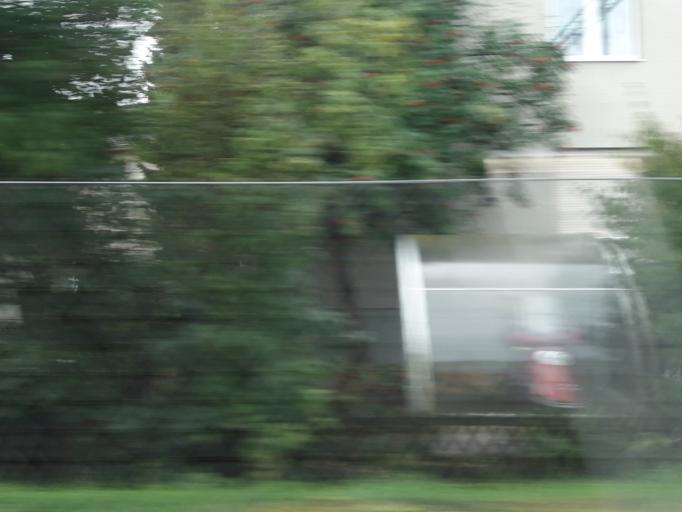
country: CH
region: Bern
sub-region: Thun District
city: Seftigen
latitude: 46.7868
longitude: 7.5392
